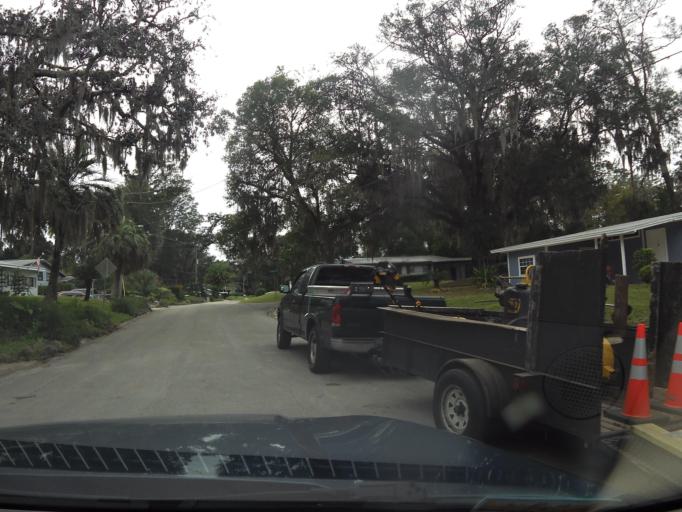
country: US
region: Florida
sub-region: Duval County
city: Jacksonville
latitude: 30.2995
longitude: -81.5962
